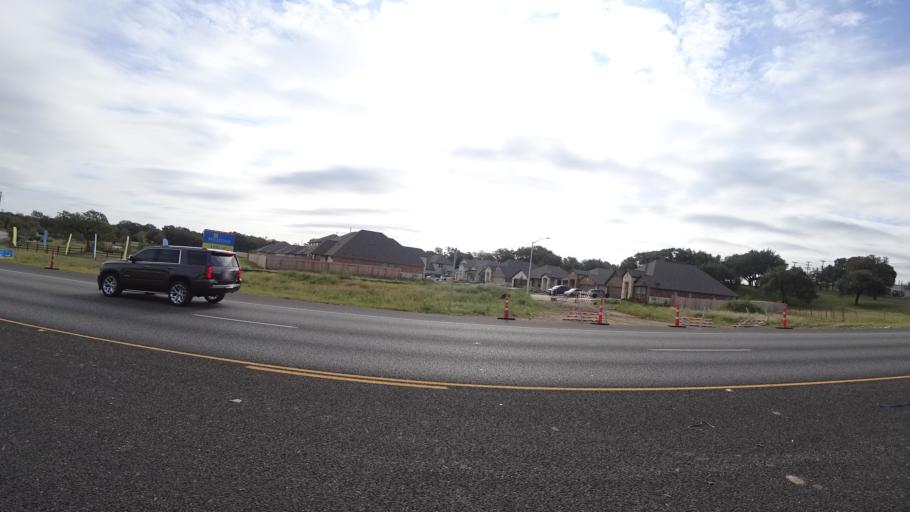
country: US
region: Texas
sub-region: Travis County
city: Manchaca
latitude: 30.1378
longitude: -97.8499
